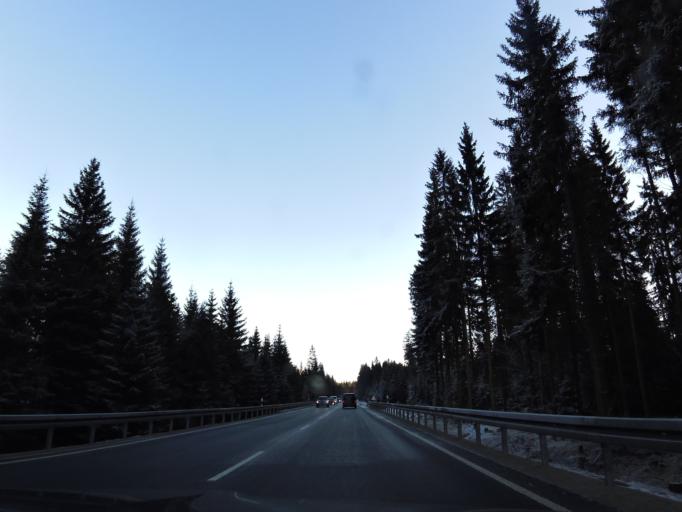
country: DE
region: Bavaria
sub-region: Upper Franconia
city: Fichtelberg
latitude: 50.0362
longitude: 11.8417
